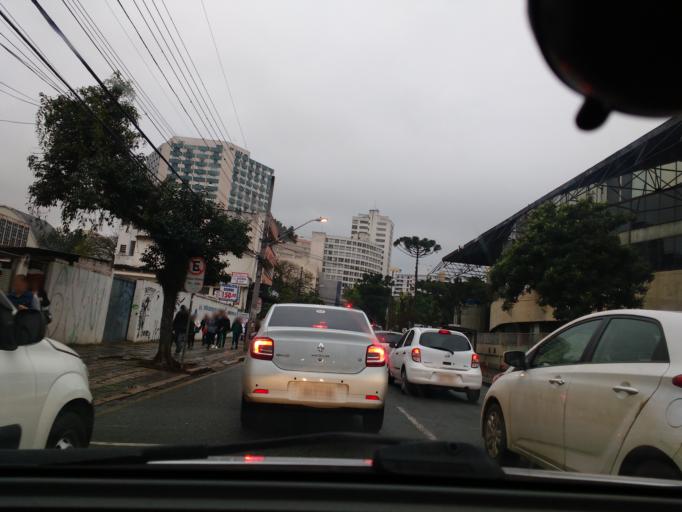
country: BR
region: Parana
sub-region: Curitiba
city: Curitiba
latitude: -25.4262
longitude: -49.2634
